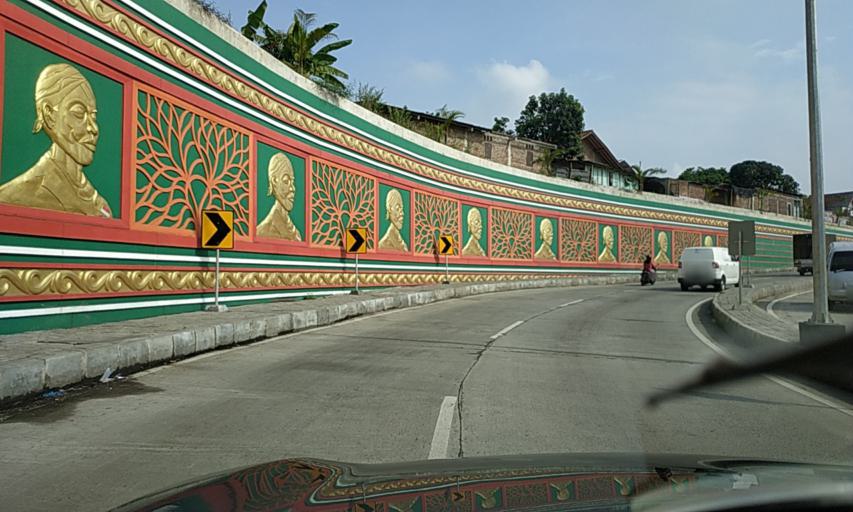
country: ID
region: Central Java
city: Purwokerto
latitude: -7.4257
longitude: 109.2222
